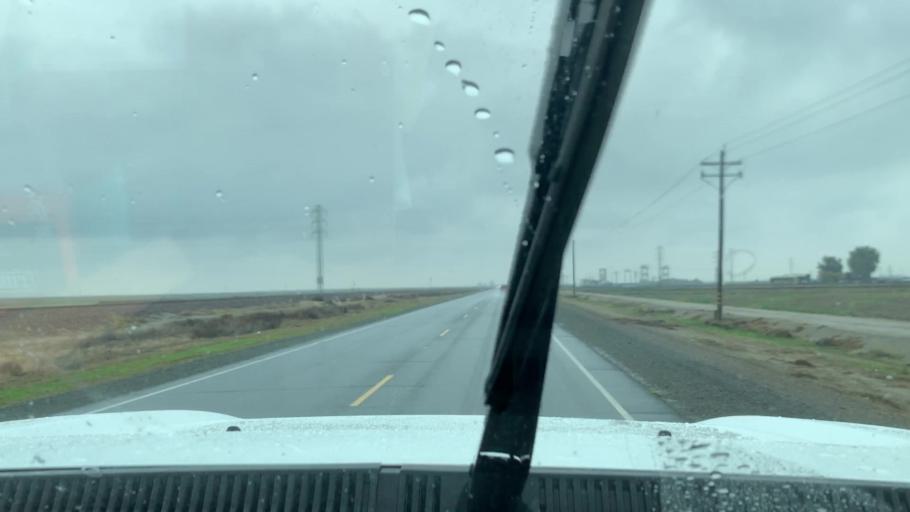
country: US
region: California
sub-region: Tulare County
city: Alpaugh
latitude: 35.9585
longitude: -119.4543
